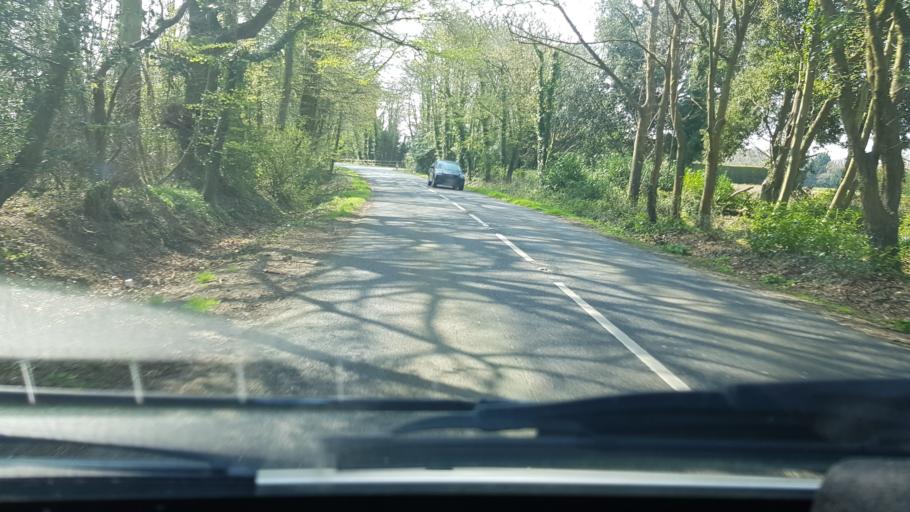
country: GB
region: England
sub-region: West Sussex
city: Chichester
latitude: 50.8511
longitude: -0.8099
